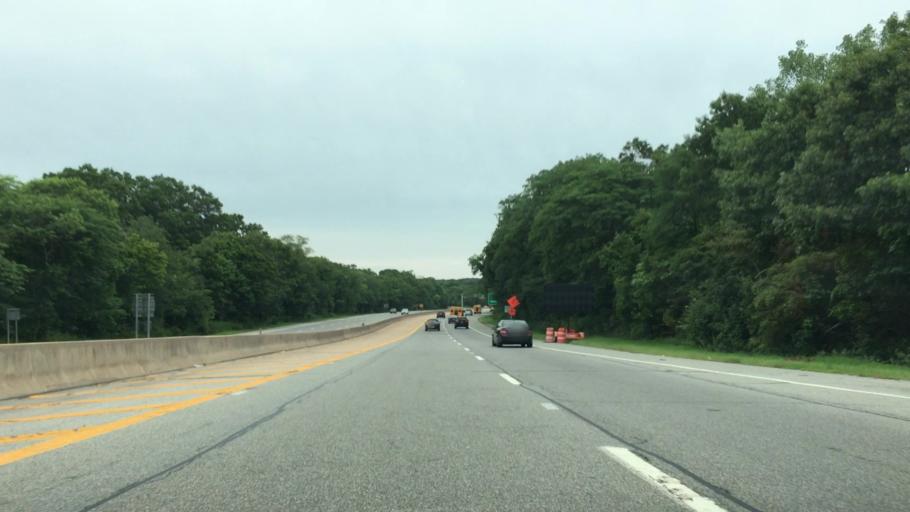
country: US
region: New York
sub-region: Nassau County
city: Syosset
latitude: 40.8050
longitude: -73.4905
